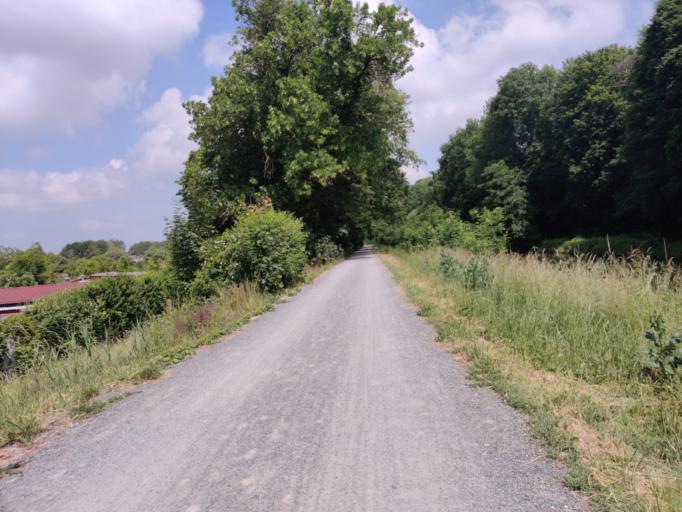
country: DE
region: Lower Saxony
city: Hildesheim
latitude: 52.1344
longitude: 9.9571
